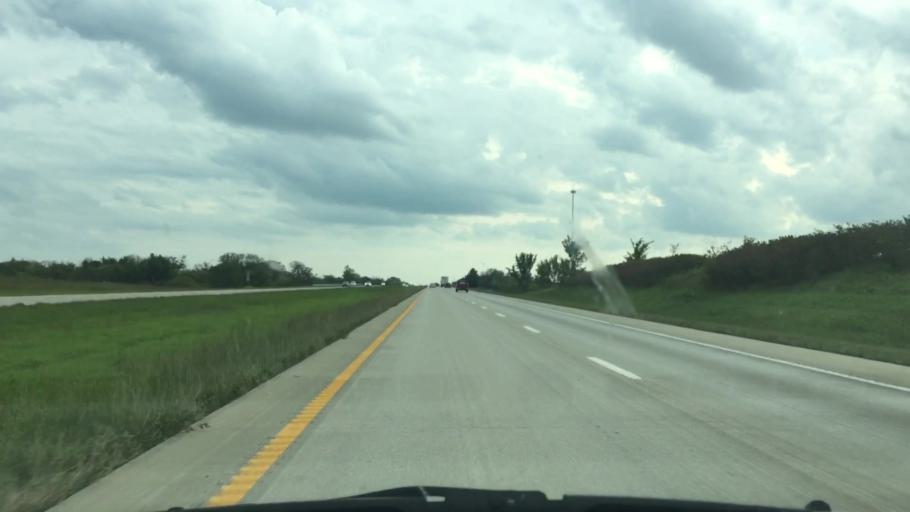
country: US
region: Missouri
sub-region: Clinton County
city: Lathrop
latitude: 39.6175
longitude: -94.2492
